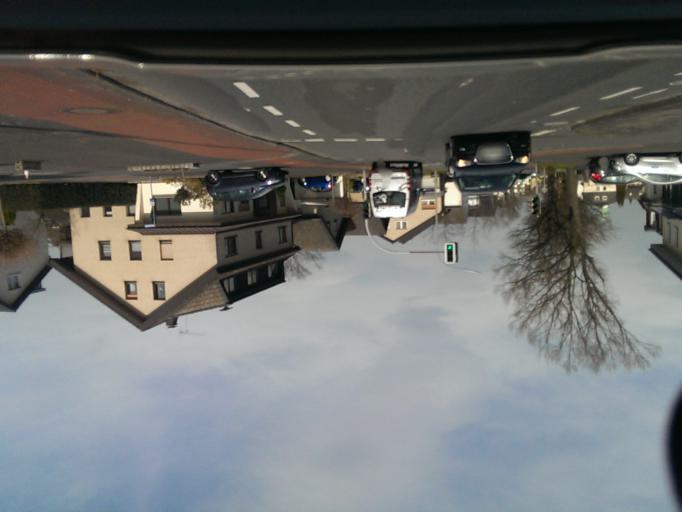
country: DE
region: North Rhine-Westphalia
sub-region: Regierungsbezirk Detmold
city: Hovelhof
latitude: 51.8184
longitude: 8.6534
